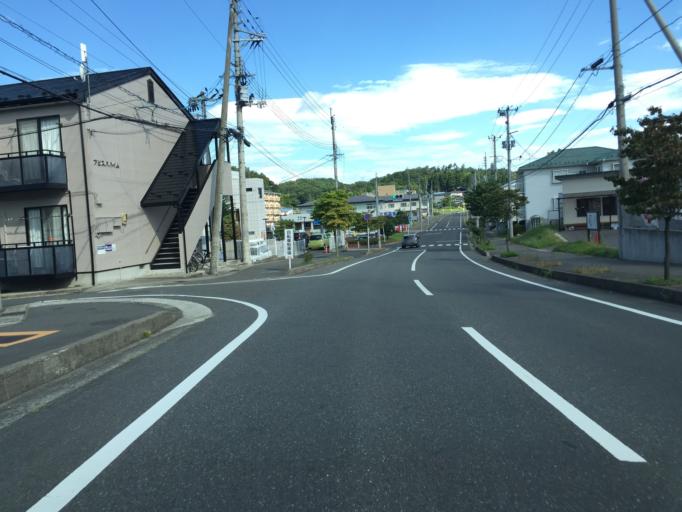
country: JP
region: Fukushima
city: Fukushima-shi
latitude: 37.6800
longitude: 140.4533
